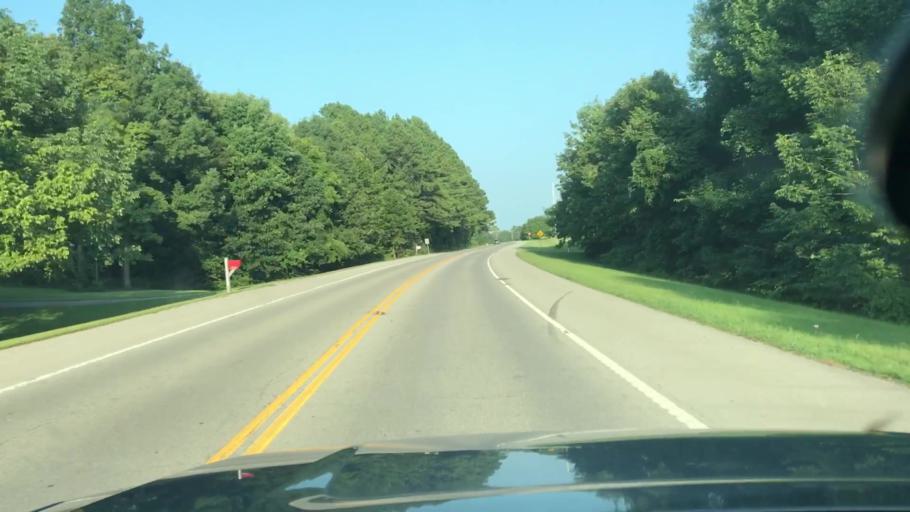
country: US
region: Tennessee
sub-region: Sumner County
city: Portland
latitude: 36.5780
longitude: -86.4473
